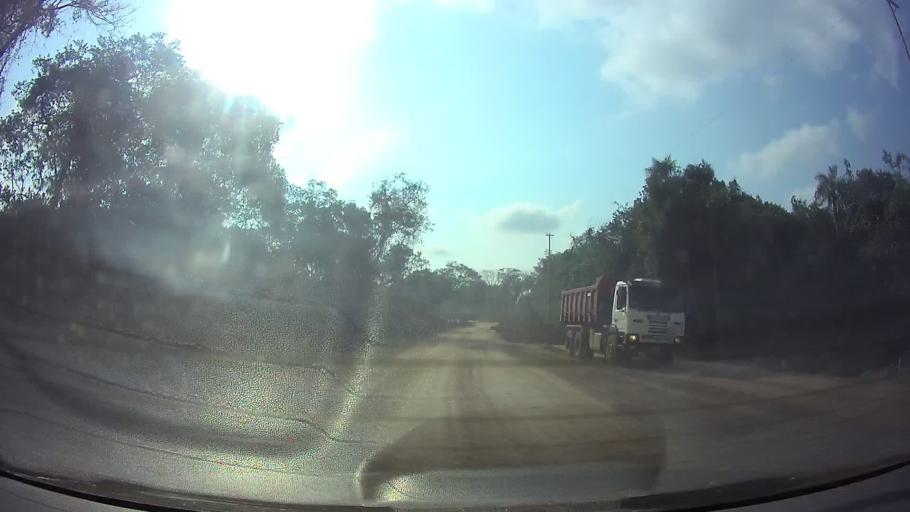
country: PY
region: Cordillera
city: Arroyos y Esteros
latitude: -25.0590
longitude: -57.1710
